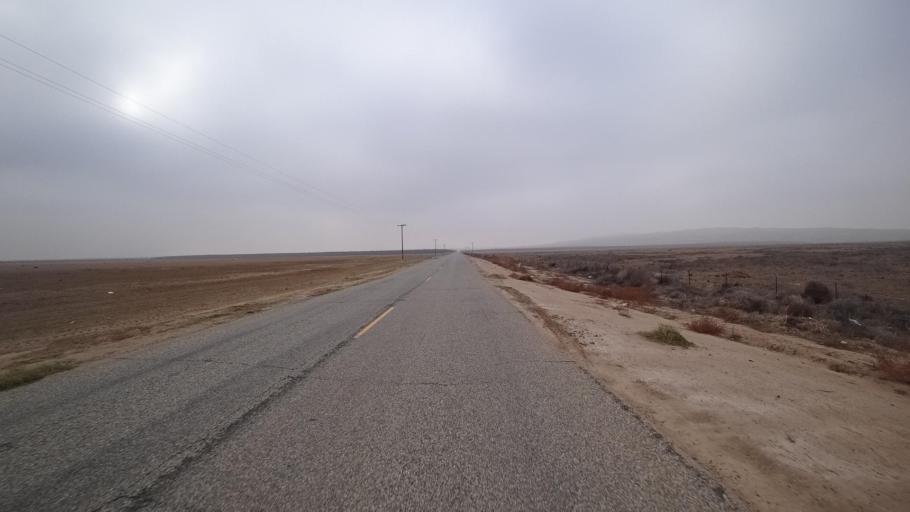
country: US
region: California
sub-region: Kern County
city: Maricopa
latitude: 35.1231
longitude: -119.3322
